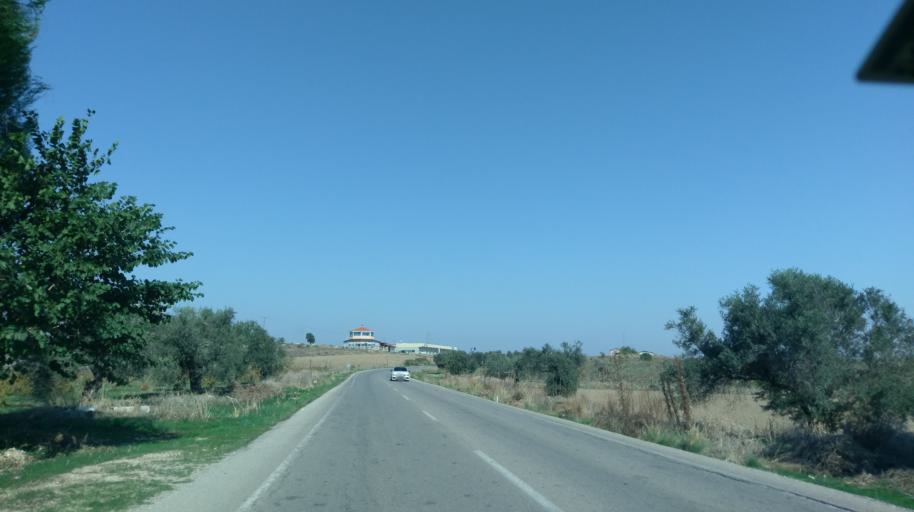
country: CY
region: Ammochostos
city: Leonarisso
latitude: 35.3744
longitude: 34.0352
